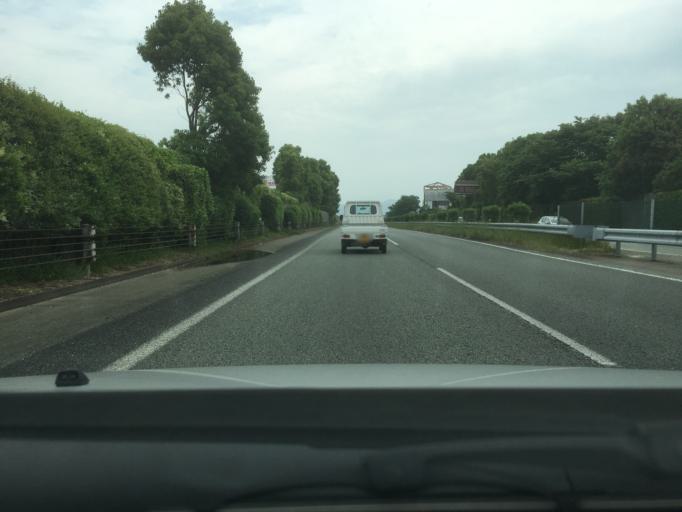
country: JP
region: Kumamoto
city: Ozu
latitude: 32.8312
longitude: 130.7816
